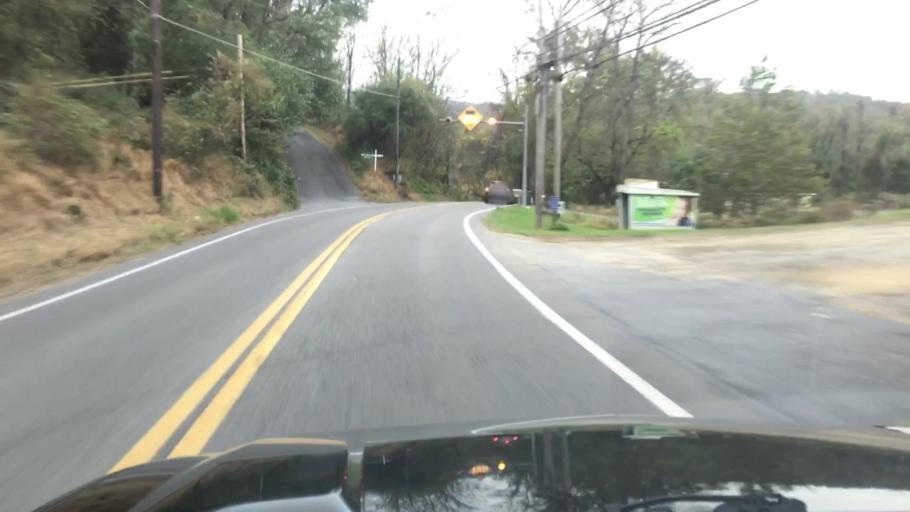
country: US
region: Pennsylvania
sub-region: Cumberland County
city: Mechanicsburg
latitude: 40.1690
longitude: -76.9793
